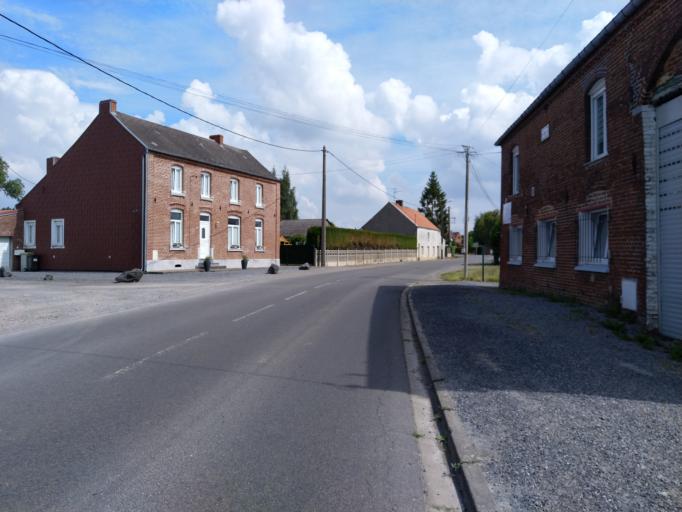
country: FR
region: Nord-Pas-de-Calais
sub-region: Departement du Nord
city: Rousies
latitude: 50.2999
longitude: 3.9946
